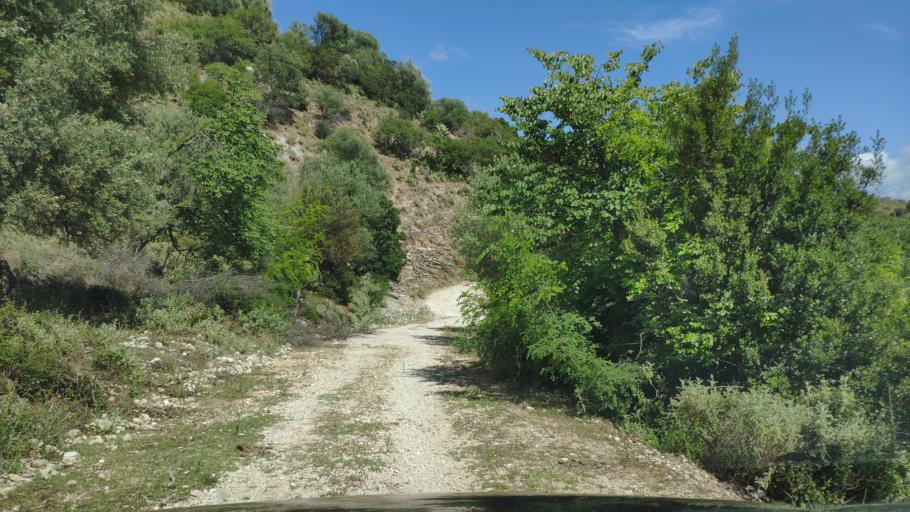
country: AL
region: Vlore
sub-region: Rrethi i Sarandes
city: Konispol
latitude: 39.6377
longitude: 20.2049
